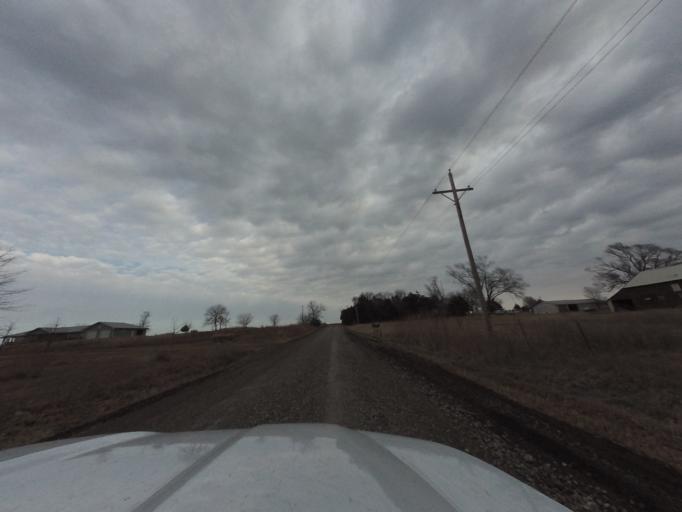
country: US
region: Kansas
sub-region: Chase County
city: Cottonwood Falls
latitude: 38.4391
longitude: -96.3731
